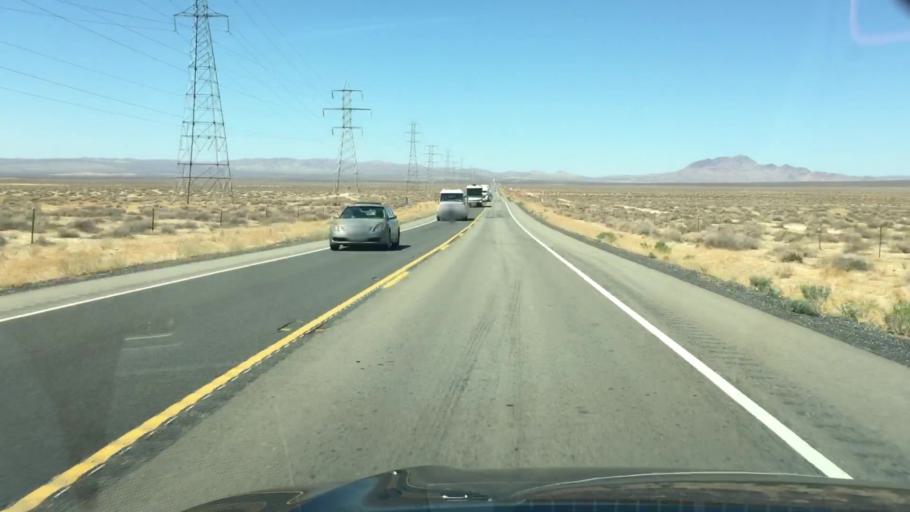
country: US
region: California
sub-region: Kern County
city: Boron
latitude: 35.1645
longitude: -117.5896
